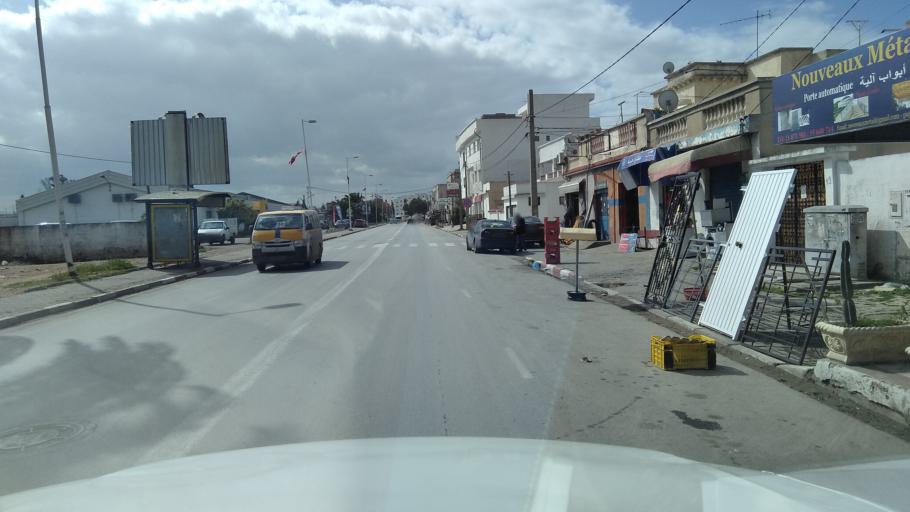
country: TN
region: Bin 'Arus
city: Ben Arous
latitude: 36.7470
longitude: 10.2258
